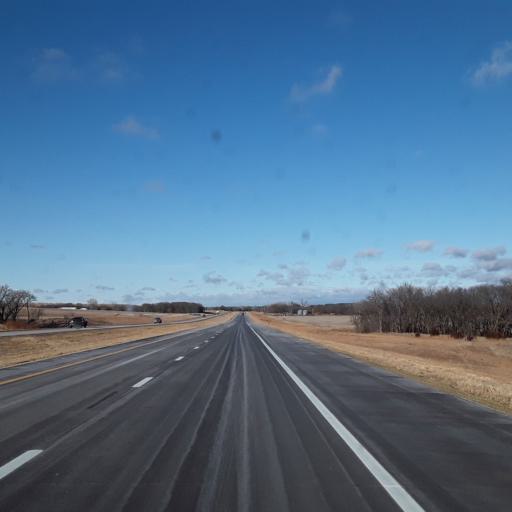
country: US
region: Kansas
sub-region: Republic County
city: Belleville
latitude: 39.7120
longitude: -97.6603
